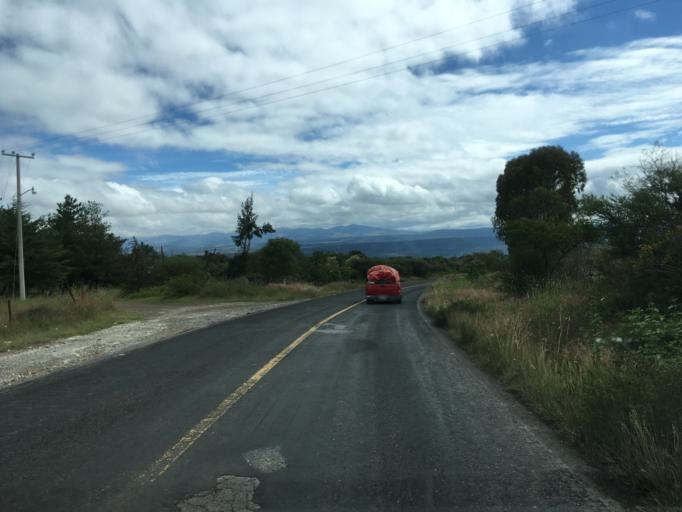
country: MX
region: Hidalgo
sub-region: Atotonilco el Grande
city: Santa Maria Amajac
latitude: 20.4118
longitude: -98.6994
